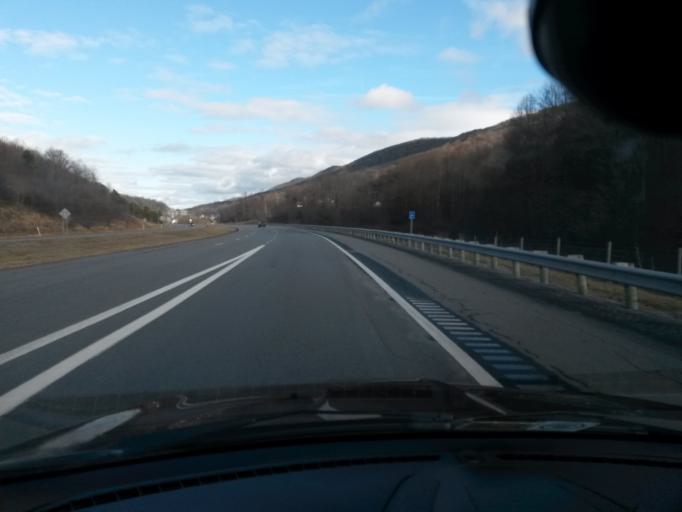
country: US
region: West Virginia
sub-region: Mercer County
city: Bluefield
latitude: 37.2736
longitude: -81.1606
